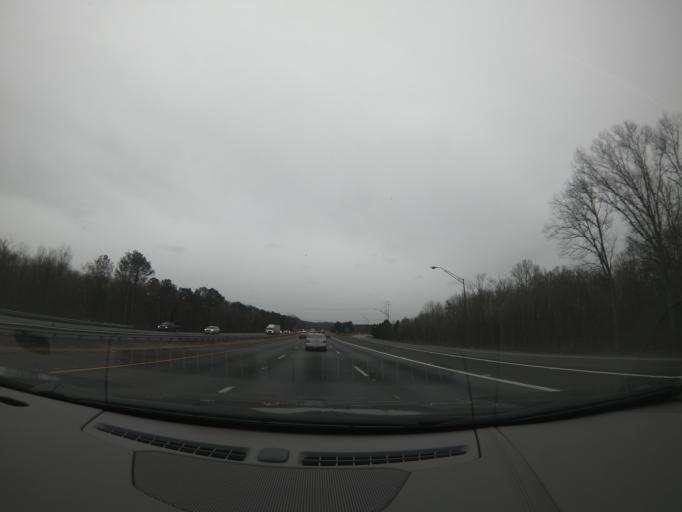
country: US
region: Georgia
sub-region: Catoosa County
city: Indian Springs
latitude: 34.9536
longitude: -85.1784
